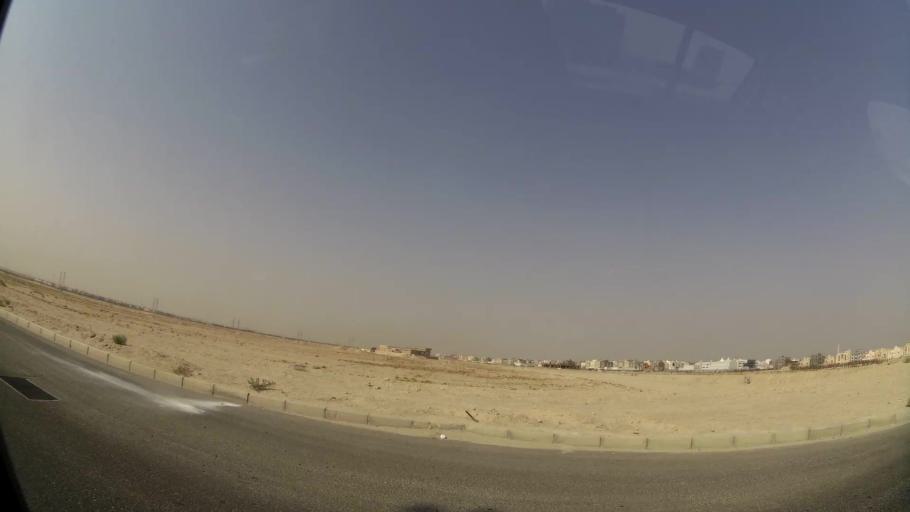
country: KW
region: Muhafazat al Jahra'
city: Al Jahra'
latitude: 29.3409
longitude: 47.7609
